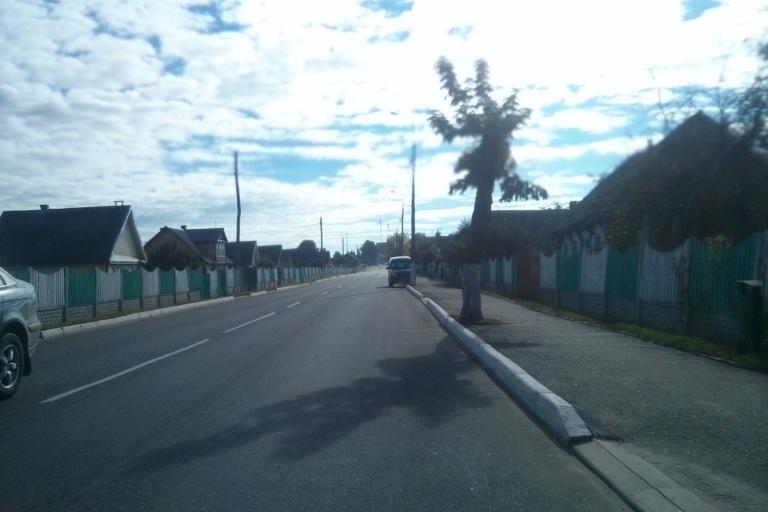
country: BY
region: Minsk
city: Chervyen'
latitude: 53.7170
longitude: 28.4080
